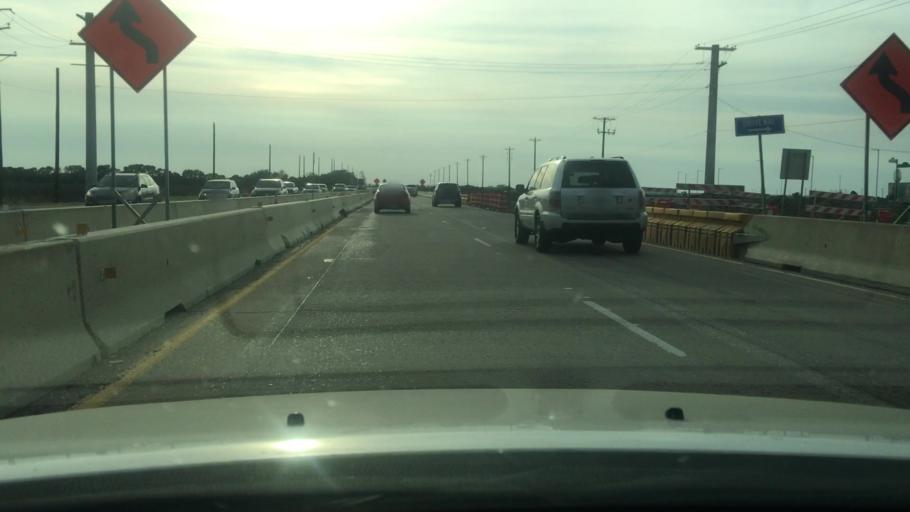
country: US
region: Texas
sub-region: Collin County
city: Prosper
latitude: 33.2193
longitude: -96.8337
